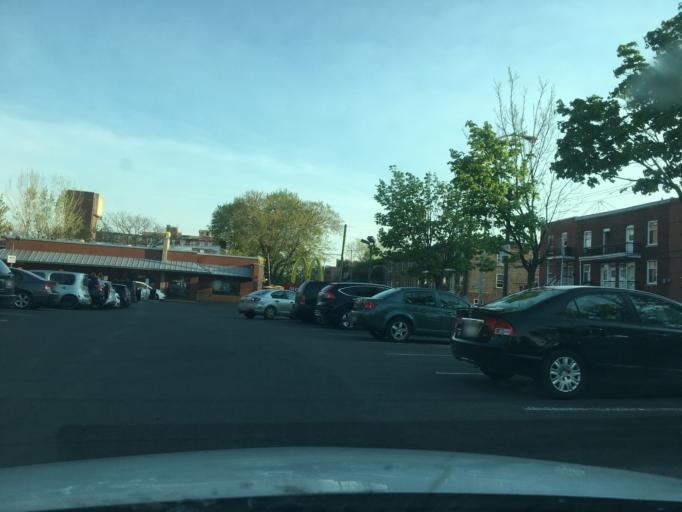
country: CA
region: Quebec
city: Westmount
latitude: 45.4614
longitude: -73.5628
